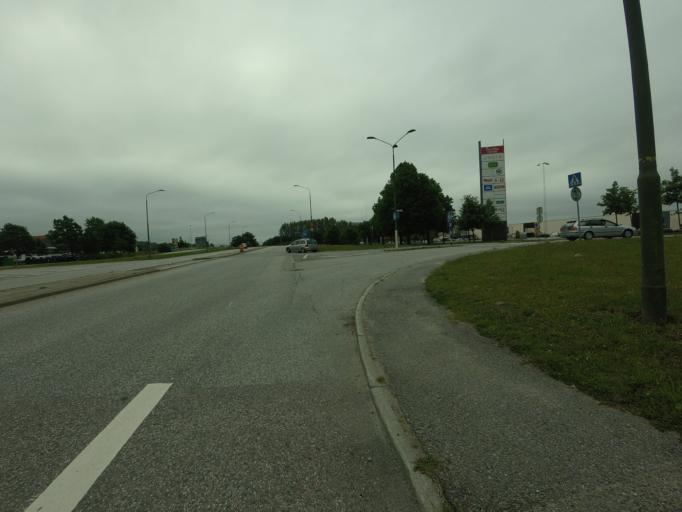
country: SE
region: Skane
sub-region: Burlovs Kommun
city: Arloev
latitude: 55.6419
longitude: 13.0867
